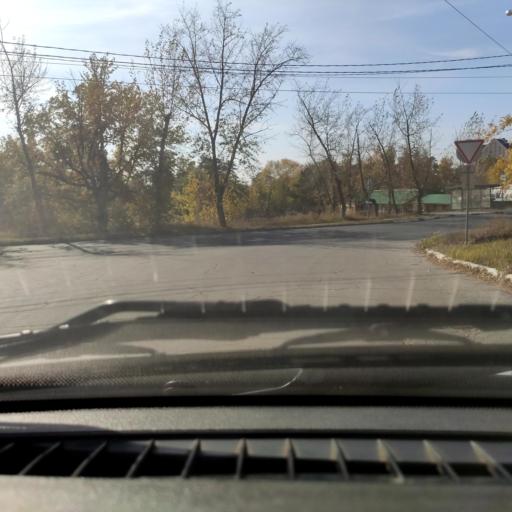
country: RU
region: Samara
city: Tol'yatti
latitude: 53.4745
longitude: 49.3785
